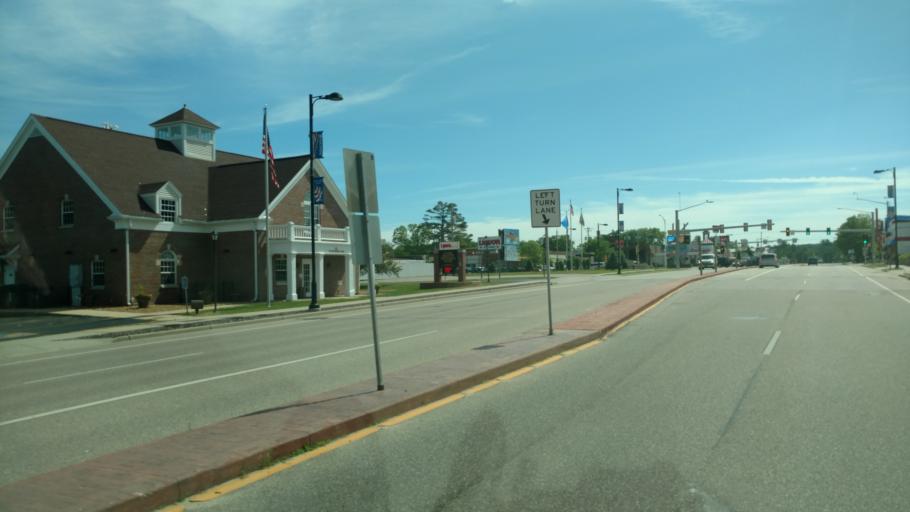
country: US
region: Wisconsin
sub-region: Sauk County
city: Lake Delton
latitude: 43.5891
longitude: -89.7956
